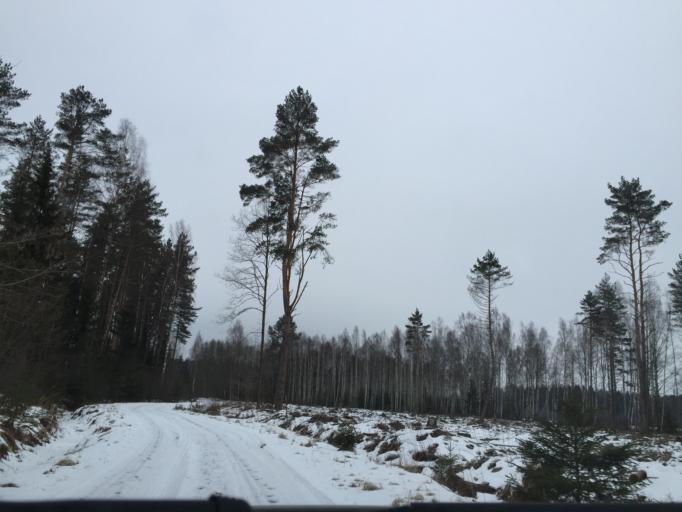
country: LV
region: Saulkrastu
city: Saulkrasti
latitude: 57.2406
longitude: 24.5076
